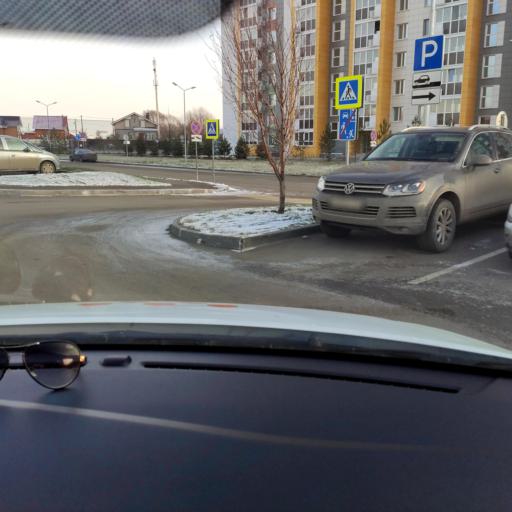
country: RU
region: Tatarstan
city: Vysokaya Gora
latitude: 55.7961
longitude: 49.2499
